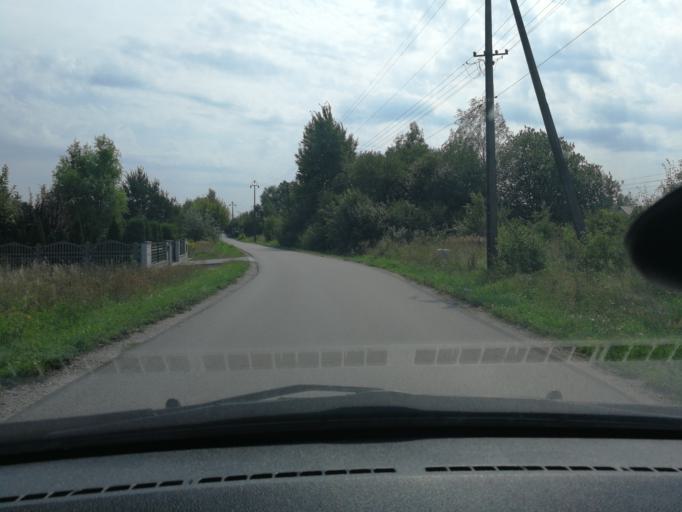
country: PL
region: Lodz Voivodeship
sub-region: Skierniewice
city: Skierniewice
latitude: 51.9721
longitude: 20.1132
